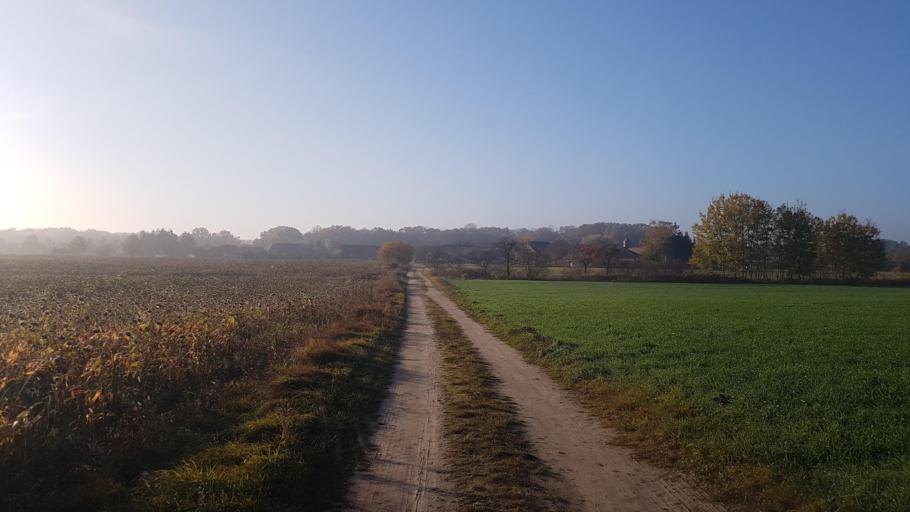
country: DE
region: Brandenburg
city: Altdobern
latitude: 51.6951
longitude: 14.0074
